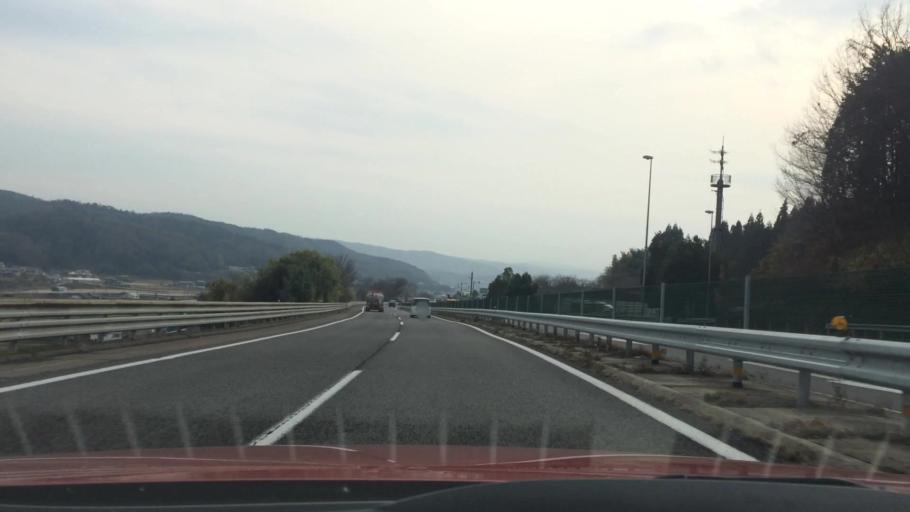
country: JP
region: Gifu
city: Mizunami
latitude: 35.3989
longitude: 137.2771
